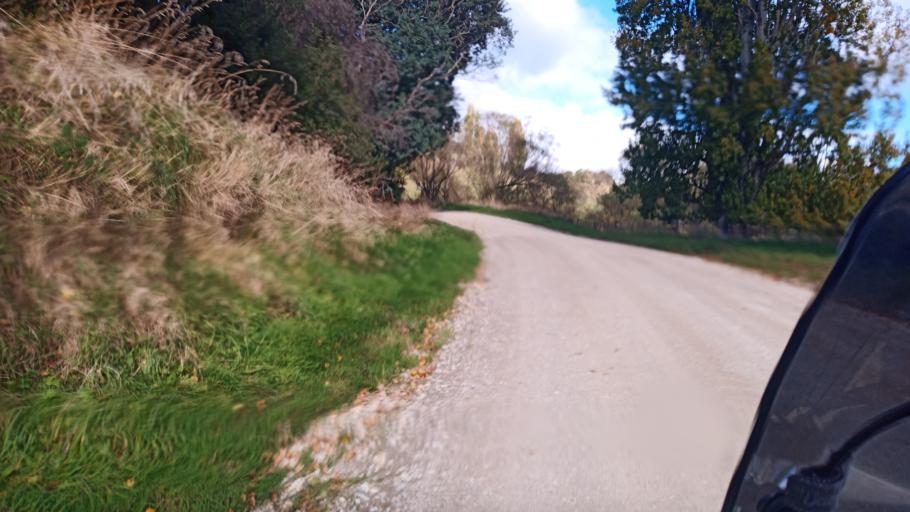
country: NZ
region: Gisborne
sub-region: Gisborne District
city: Gisborne
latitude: -38.5368
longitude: 177.5209
